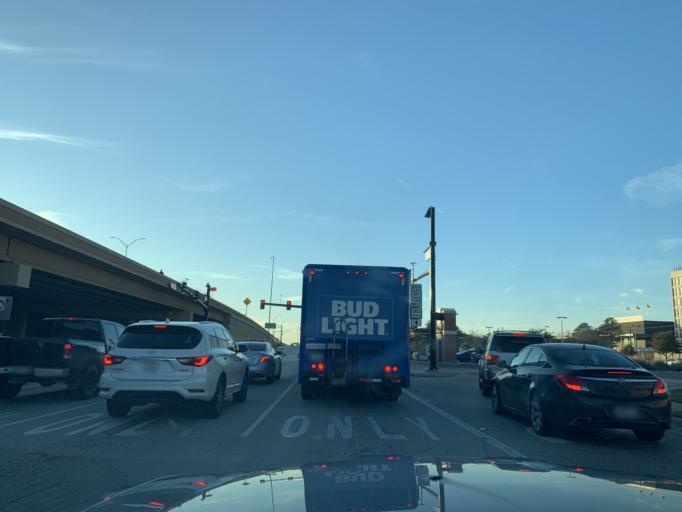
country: US
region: Texas
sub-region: Tarrant County
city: Bedford
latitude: 32.8374
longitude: -97.1330
